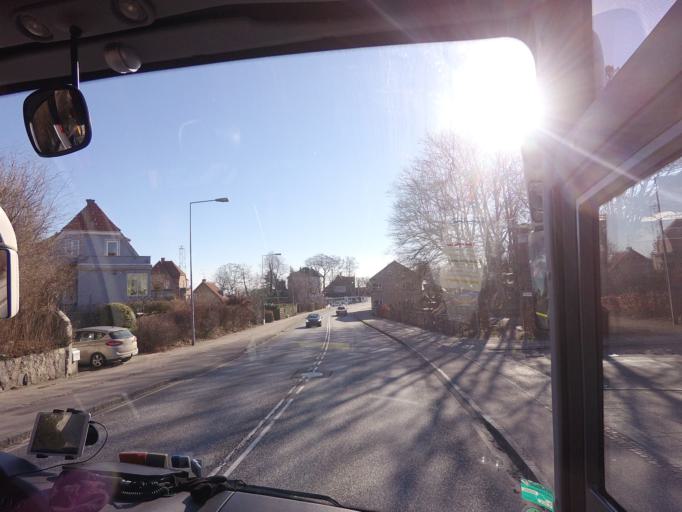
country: DK
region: Capital Region
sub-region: Helsingor Kommune
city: Helsingor
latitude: 56.0289
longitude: 12.6017
